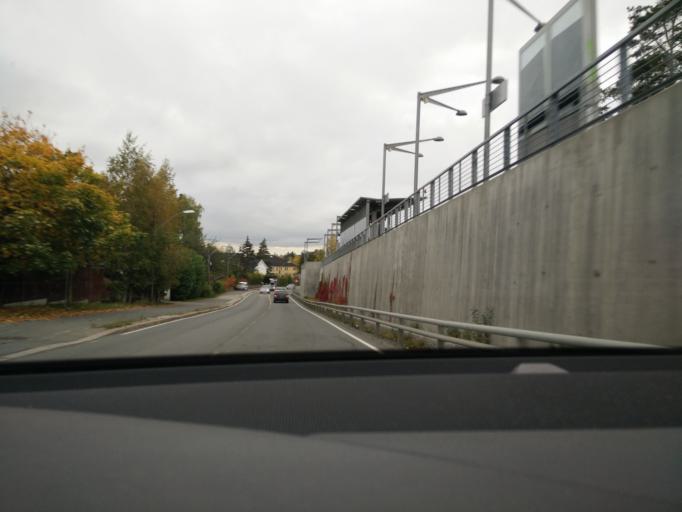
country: NO
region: Akershus
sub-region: Baerum
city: Lysaker
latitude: 59.9268
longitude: 10.6354
